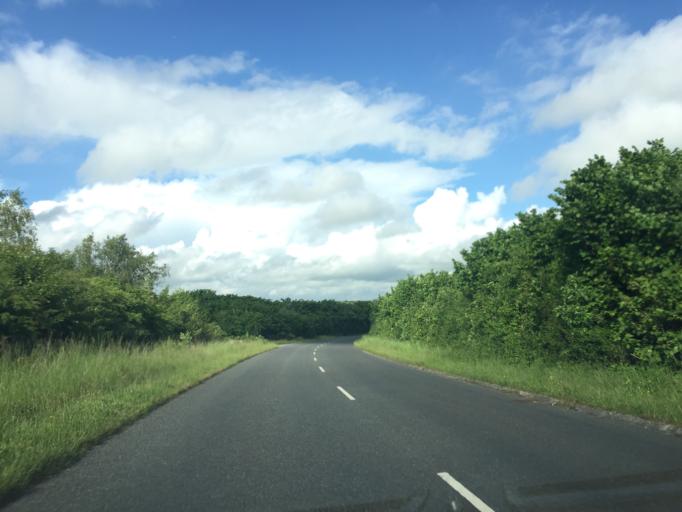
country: GB
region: England
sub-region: Dorset
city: Dorchester
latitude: 50.7459
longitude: -2.3608
